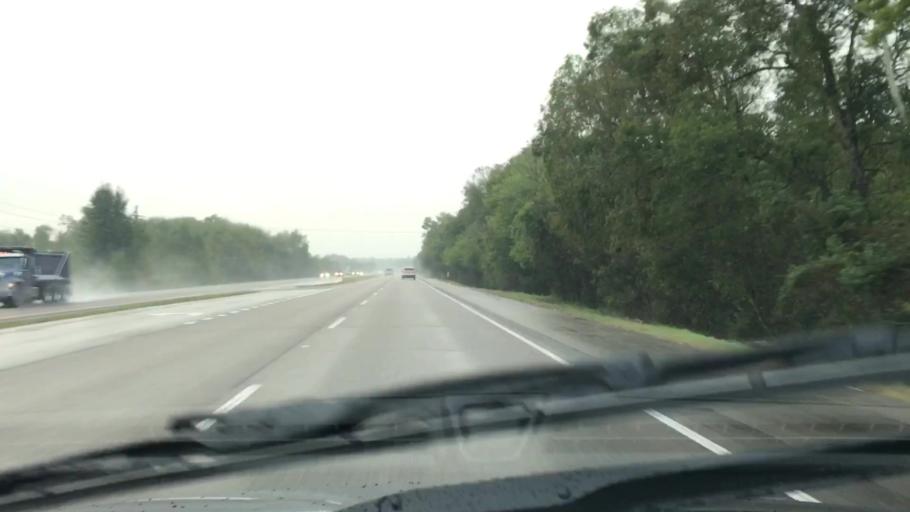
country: US
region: Louisiana
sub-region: Saint Charles Parish
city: Paradis
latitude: 29.8636
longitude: -90.4457
